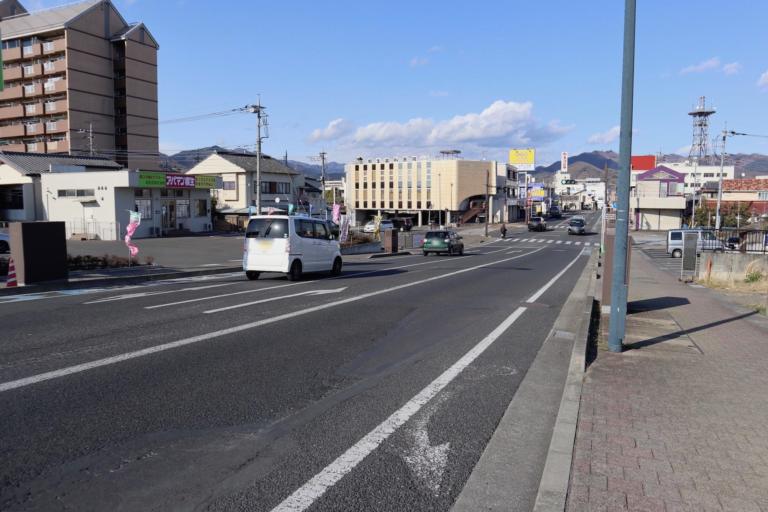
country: JP
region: Gunma
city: Kiryu
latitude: 36.4006
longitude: 139.3302
